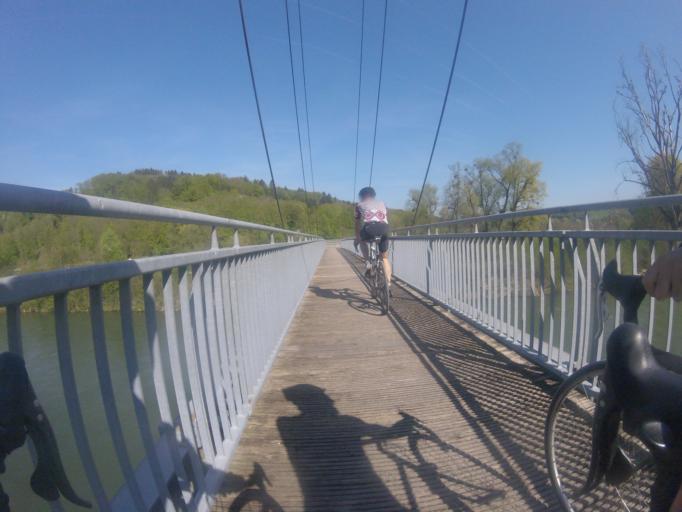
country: CH
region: Bern
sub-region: Bern-Mittelland District
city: Muhleberg
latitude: 46.9781
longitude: 7.2536
